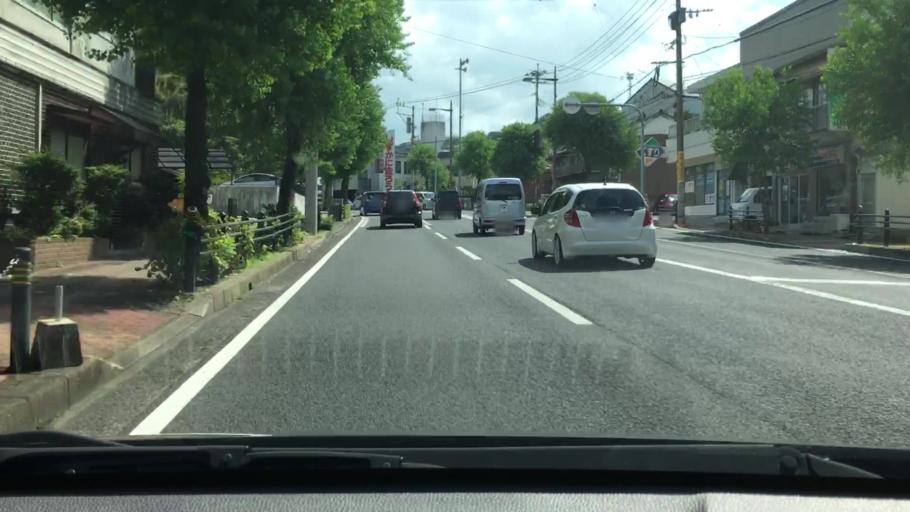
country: JP
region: Nagasaki
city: Sasebo
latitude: 33.2026
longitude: 129.7210
